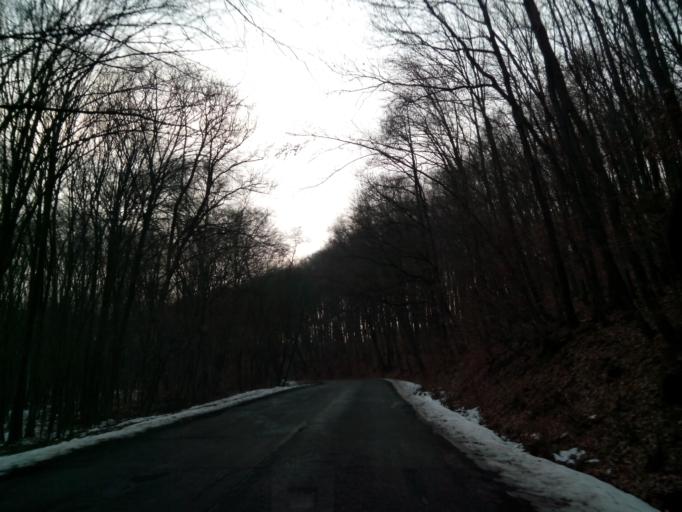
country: HU
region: Borsod-Abauj-Zemplen
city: Gonc
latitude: 48.4882
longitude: 21.4017
